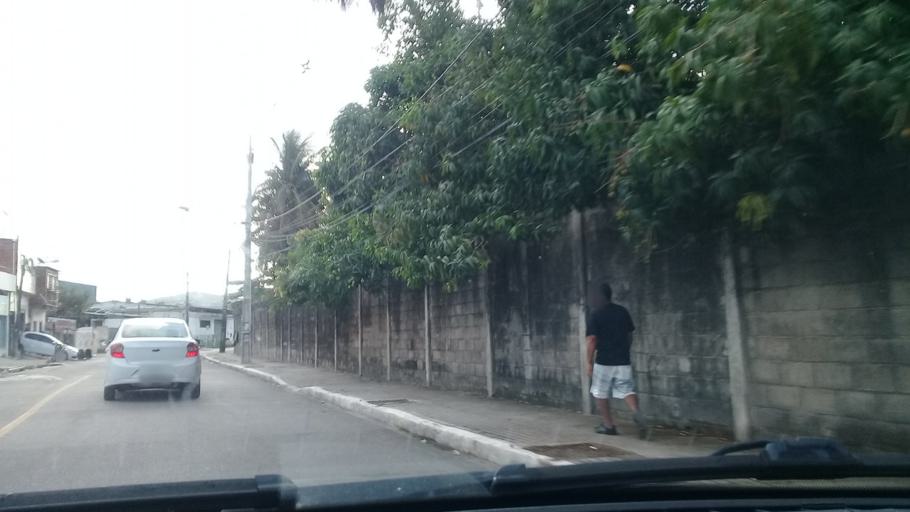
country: BR
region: Pernambuco
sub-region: Jaboatao Dos Guararapes
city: Jaboatao
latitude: -8.1404
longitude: -34.9231
